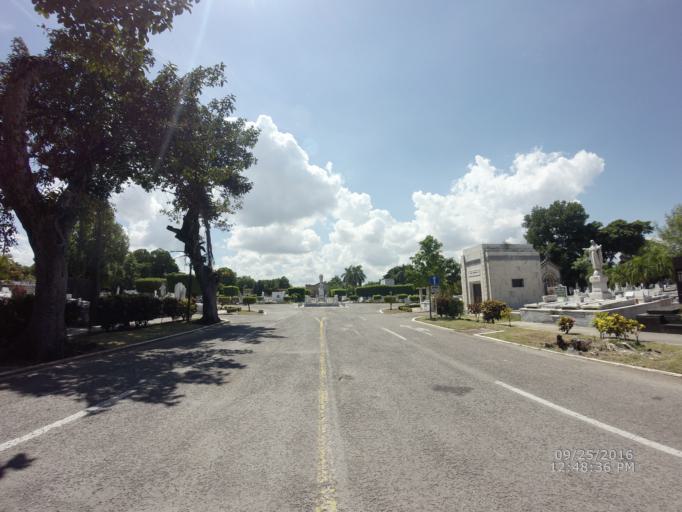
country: CU
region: La Habana
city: Havana
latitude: 23.1219
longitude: -82.3990
